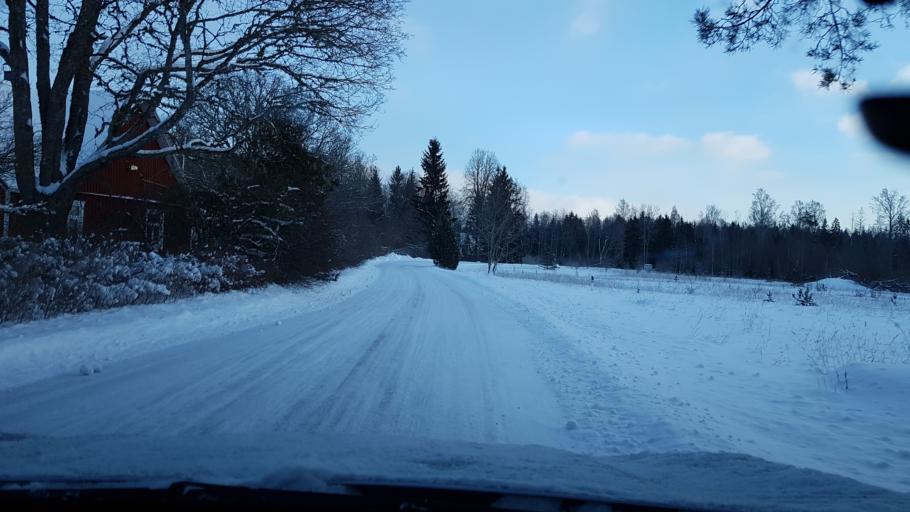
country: EE
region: Harju
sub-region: Nissi vald
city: Turba
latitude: 59.1525
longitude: 24.1473
